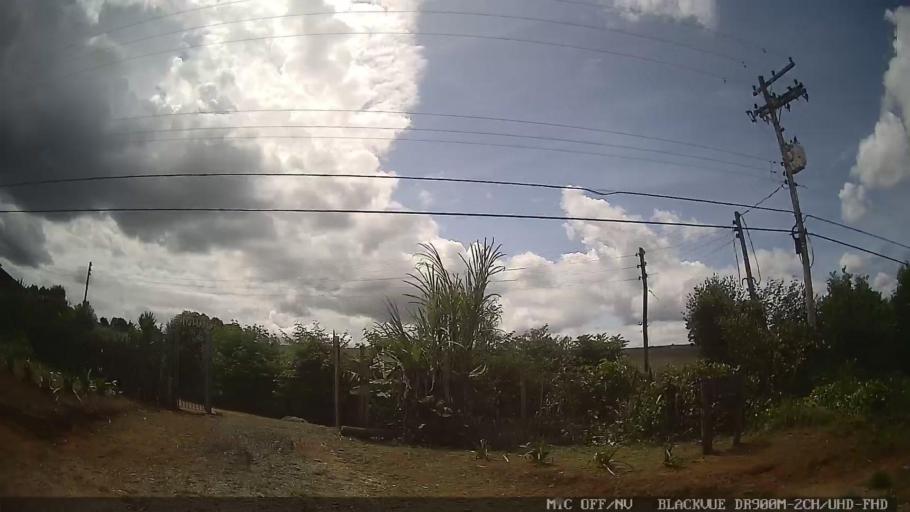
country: BR
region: Sao Paulo
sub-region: Suzano
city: Suzano
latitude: -23.6601
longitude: -46.2425
